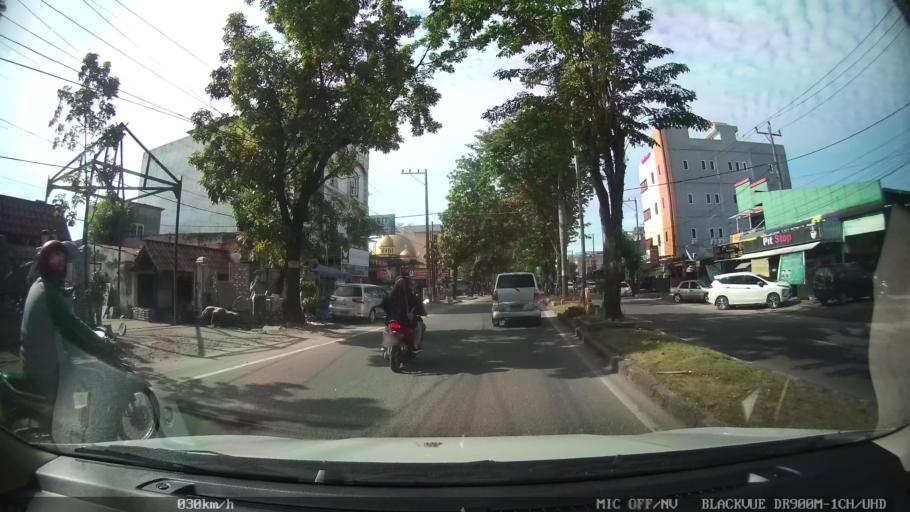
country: ID
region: North Sumatra
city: Medan
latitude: 3.5832
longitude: 98.6431
